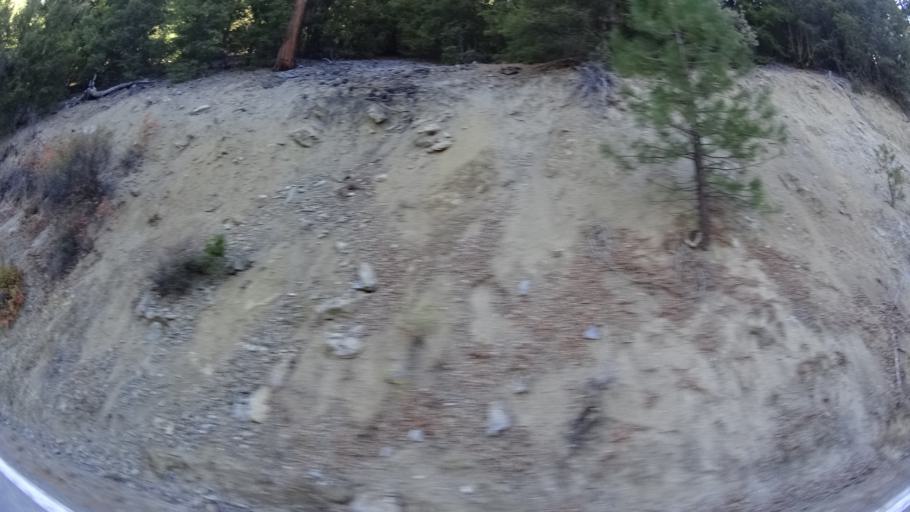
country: US
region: California
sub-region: Trinity County
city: Weaverville
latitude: 41.2217
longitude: -123.0122
